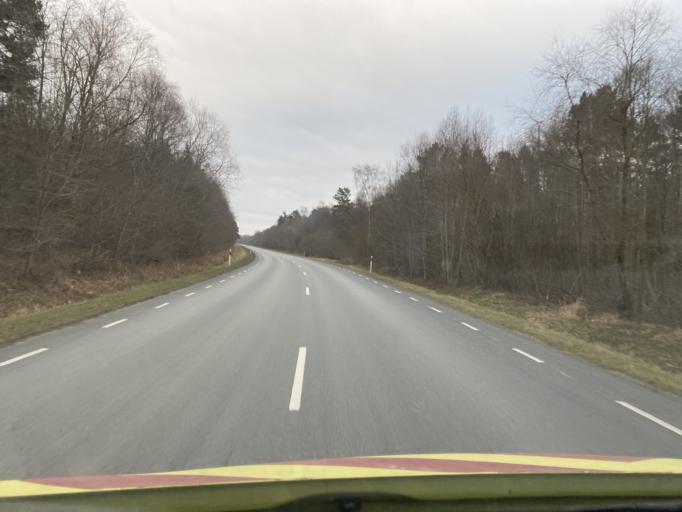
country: EE
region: Laeaene
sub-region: Ridala Parish
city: Uuemoisa
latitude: 58.8510
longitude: 23.6396
